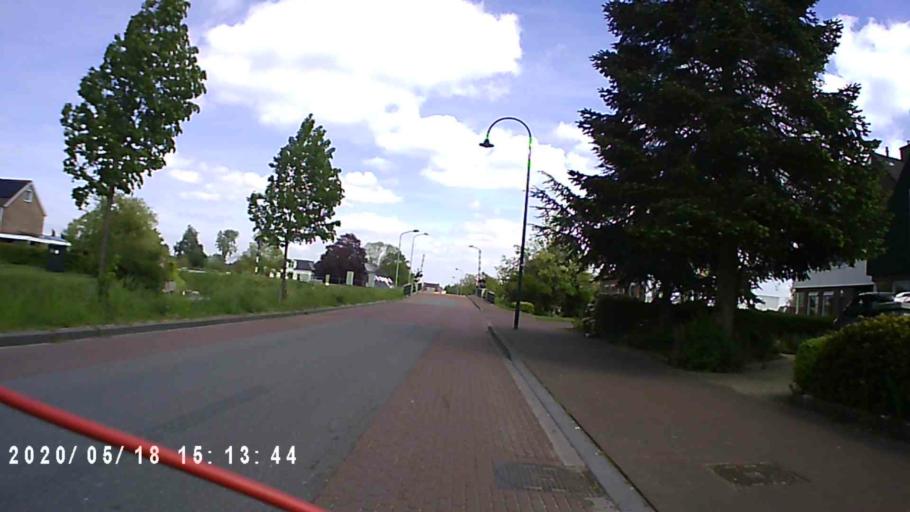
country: NL
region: Groningen
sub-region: Gemeente Winsum
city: Winsum
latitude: 53.3344
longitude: 6.5182
